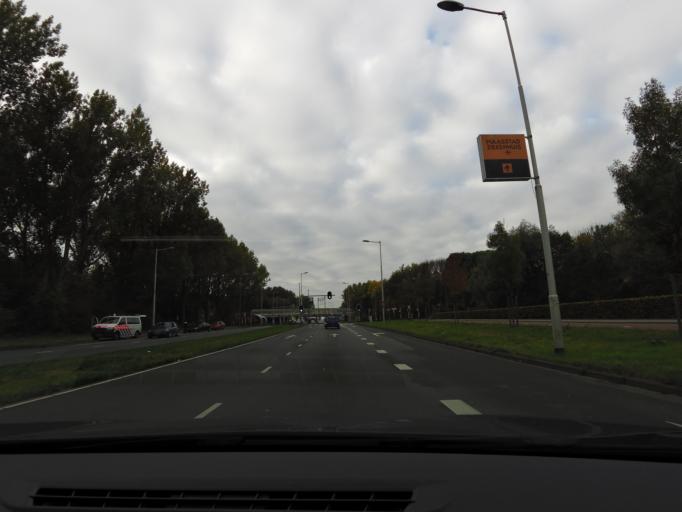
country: NL
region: South Holland
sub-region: Gemeente Rotterdam
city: Delfshaven
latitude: 51.8734
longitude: 4.4573
